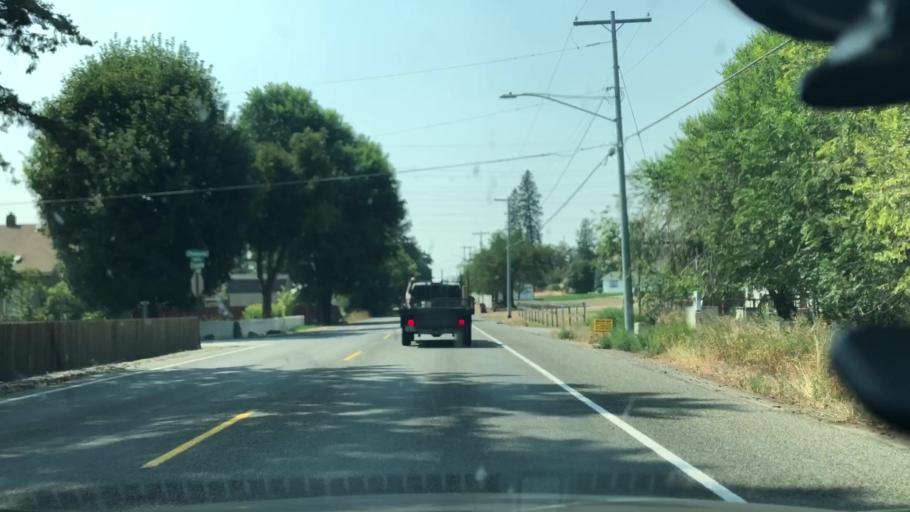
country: US
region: Washington
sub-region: Spokane County
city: Millwood
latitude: 47.6856
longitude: -117.3382
